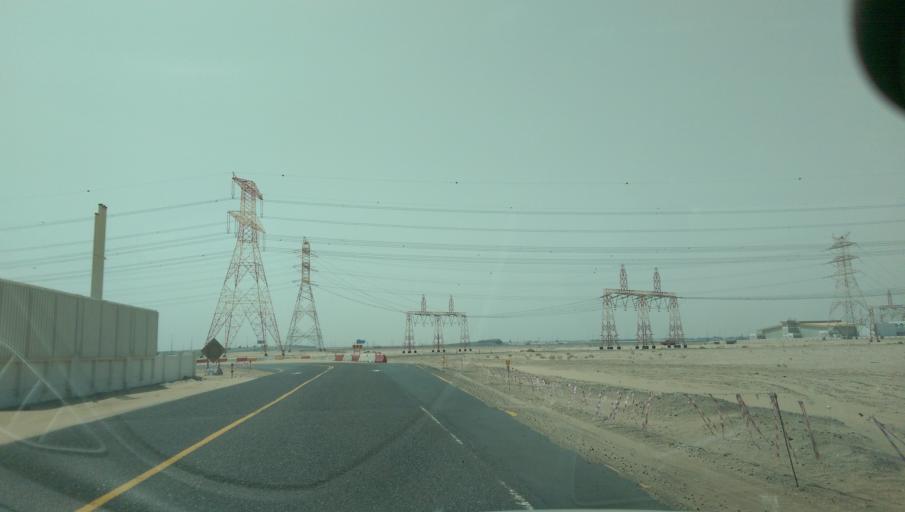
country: AE
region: Abu Dhabi
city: Abu Dhabi
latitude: 24.2959
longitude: 54.5408
